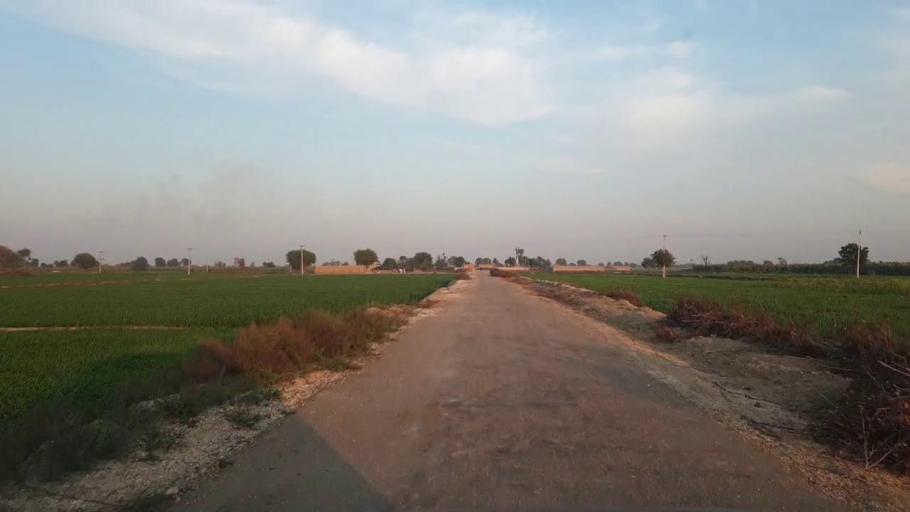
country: PK
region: Sindh
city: Shahpur Chakar
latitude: 26.1884
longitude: 68.6186
